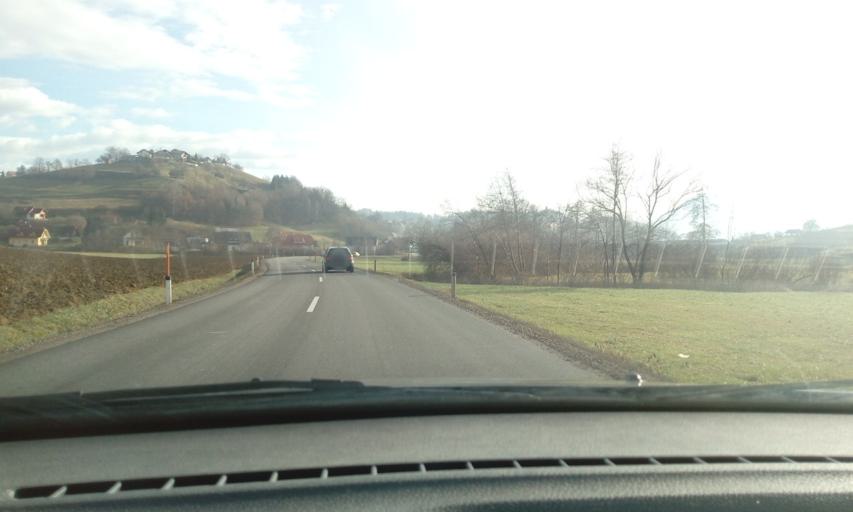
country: SI
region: Sentjur pri Celju
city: Sentjur
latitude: 46.2303
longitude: 15.3893
